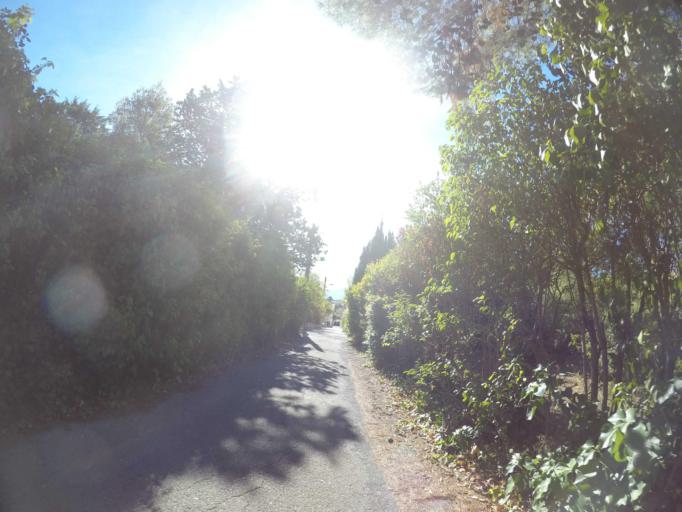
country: FR
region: Languedoc-Roussillon
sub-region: Departement des Pyrenees-Orientales
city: Trouillas
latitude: 42.6151
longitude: 2.8104
